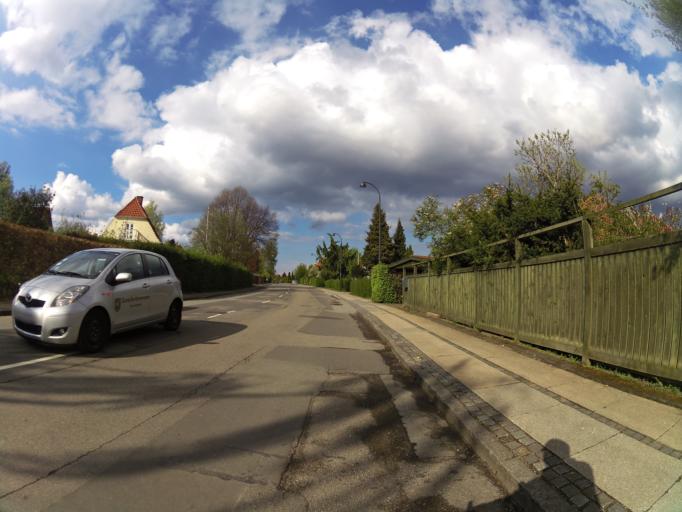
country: DK
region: Capital Region
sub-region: Lyngby-Tarbaek Kommune
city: Kongens Lyngby
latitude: 55.7302
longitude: 12.5316
